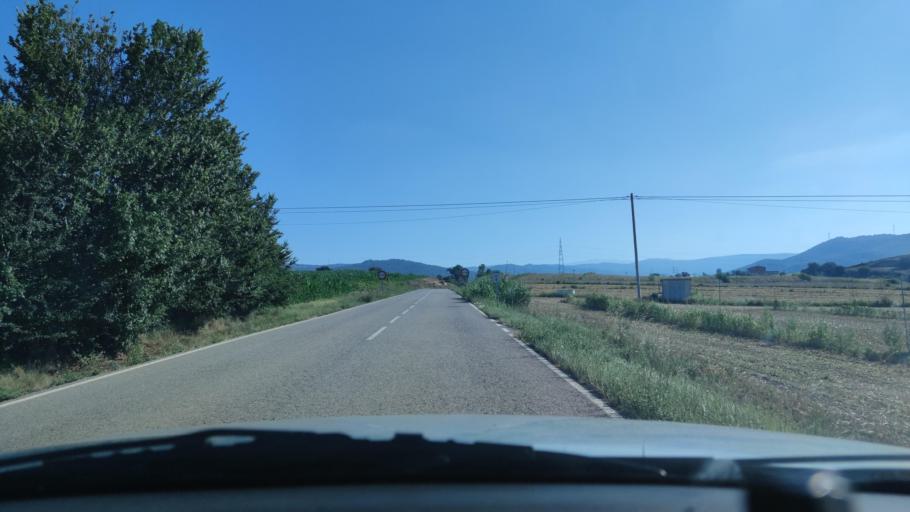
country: ES
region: Catalonia
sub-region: Provincia de Lleida
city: Ponts
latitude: 41.8973
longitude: 1.2374
